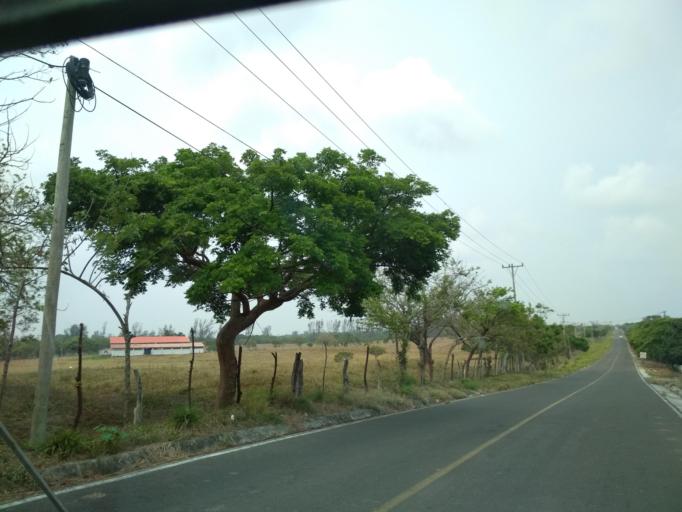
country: MX
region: Veracruz
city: Anton Lizardo
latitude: 19.0191
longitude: -95.9888
